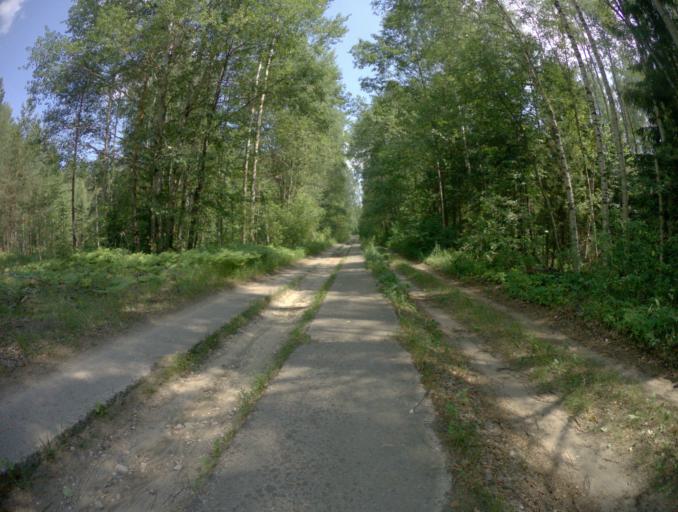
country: RU
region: Nizjnij Novgorod
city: Frolishchi
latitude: 56.4339
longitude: 42.6197
